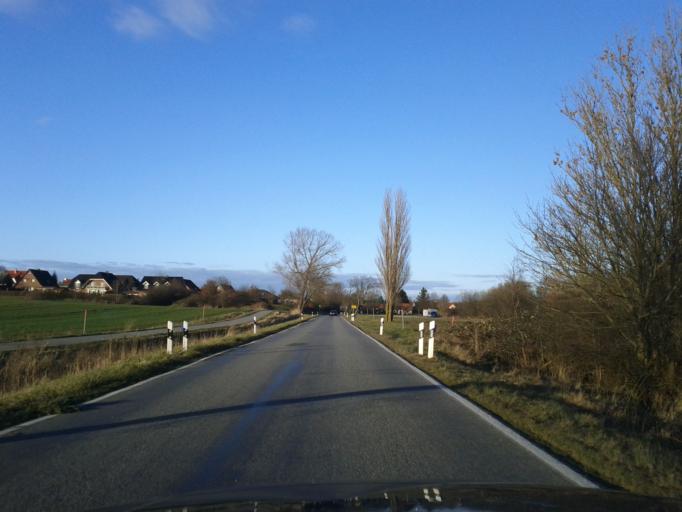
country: DE
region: Mecklenburg-Vorpommern
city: Blowatz
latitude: 53.9931
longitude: 11.4344
